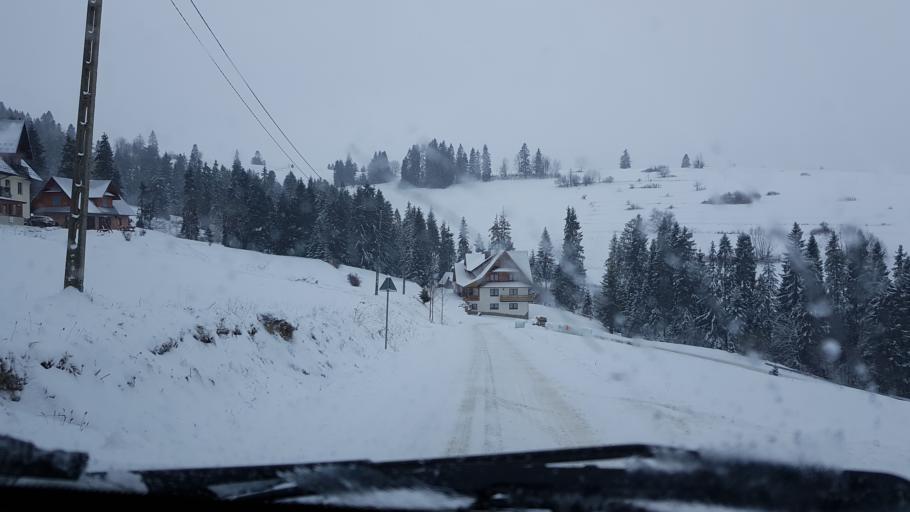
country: PL
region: Lesser Poland Voivodeship
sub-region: Powiat tatrzanski
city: Czarna Gora
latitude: 49.3577
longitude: 20.1599
